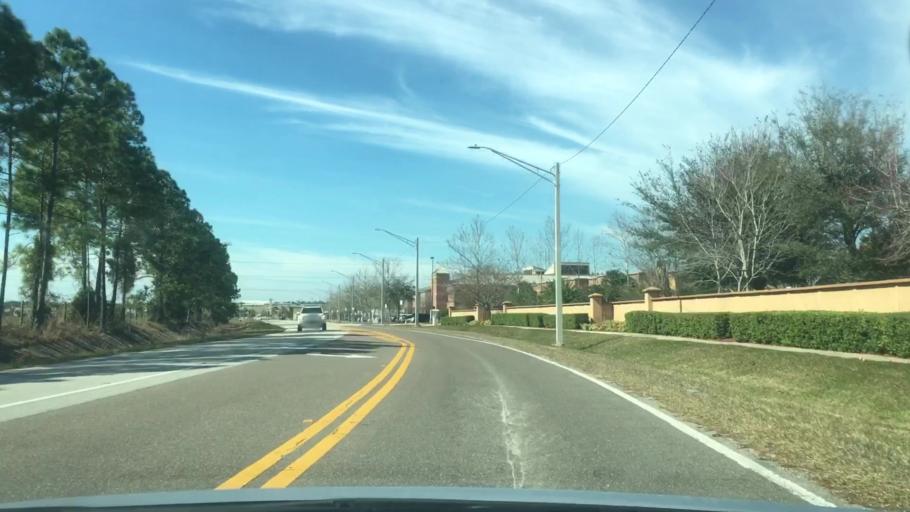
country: US
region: Florida
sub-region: Duval County
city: Atlantic Beach
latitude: 30.3222
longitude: -81.4851
